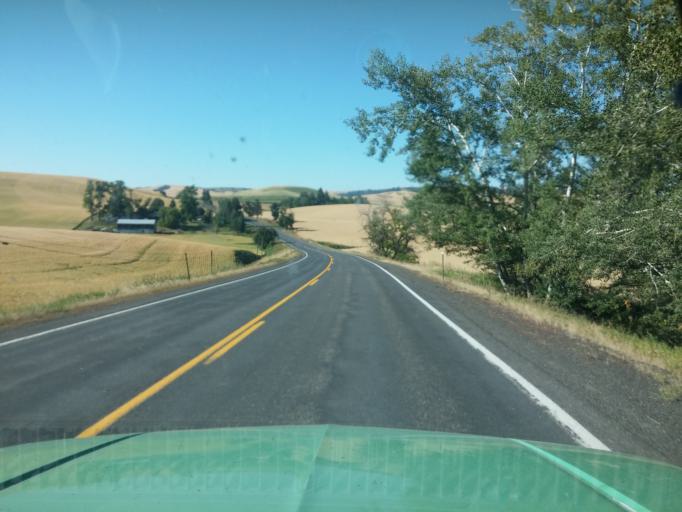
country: US
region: Idaho
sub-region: Latah County
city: Moscow
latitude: 46.6845
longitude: -117.0218
